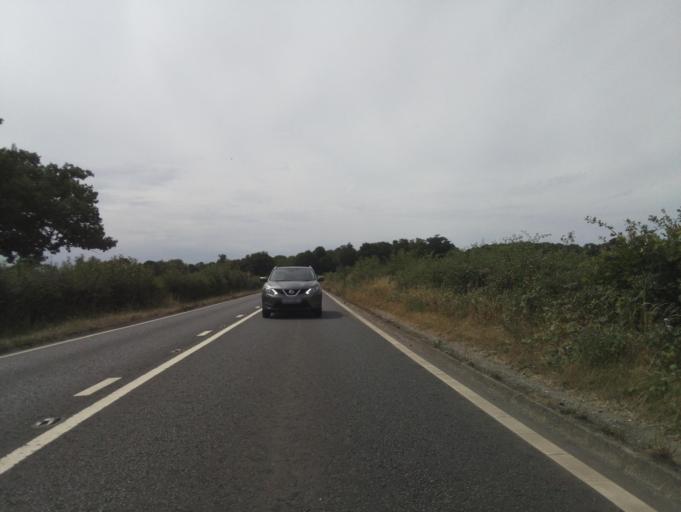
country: GB
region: England
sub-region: Surrey
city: Salfords
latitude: 51.2037
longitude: -0.1977
